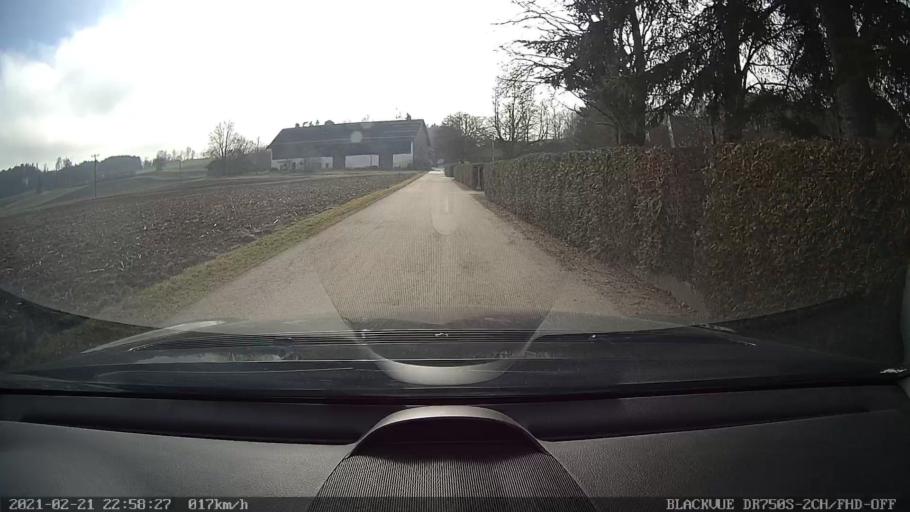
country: DE
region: Bavaria
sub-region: Upper Bavaria
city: Griesstatt
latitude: 48.0078
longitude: 12.1774
